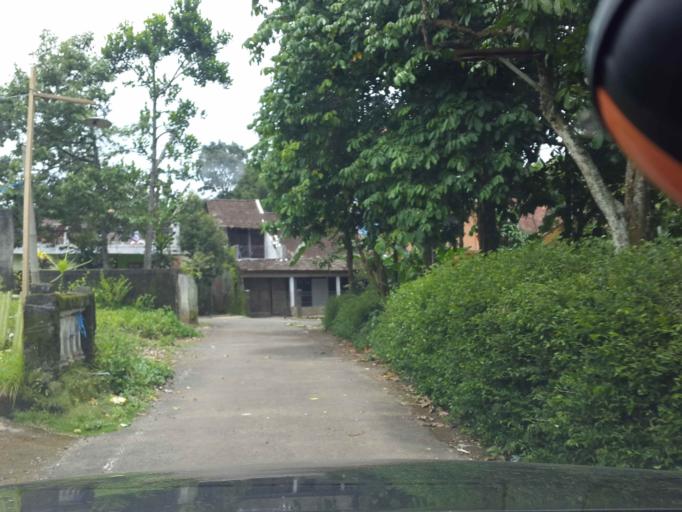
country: ID
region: Central Java
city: Salatiga
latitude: -7.3424
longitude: 110.4797
